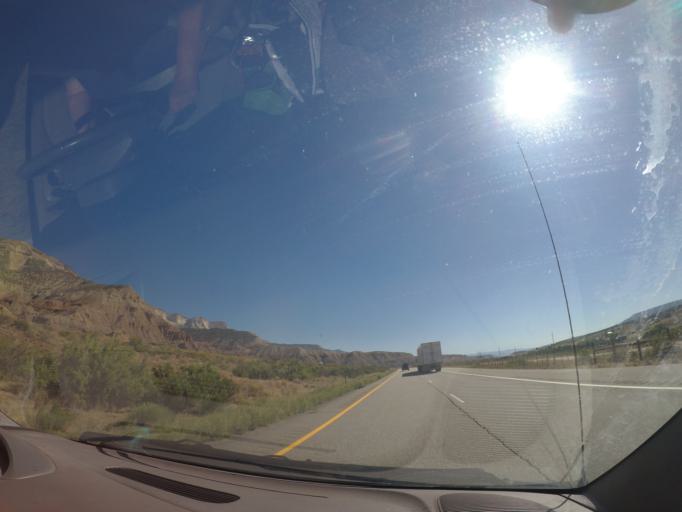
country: US
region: Colorado
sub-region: Garfield County
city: Battlement Mesa
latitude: 39.4899
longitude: -107.9531
